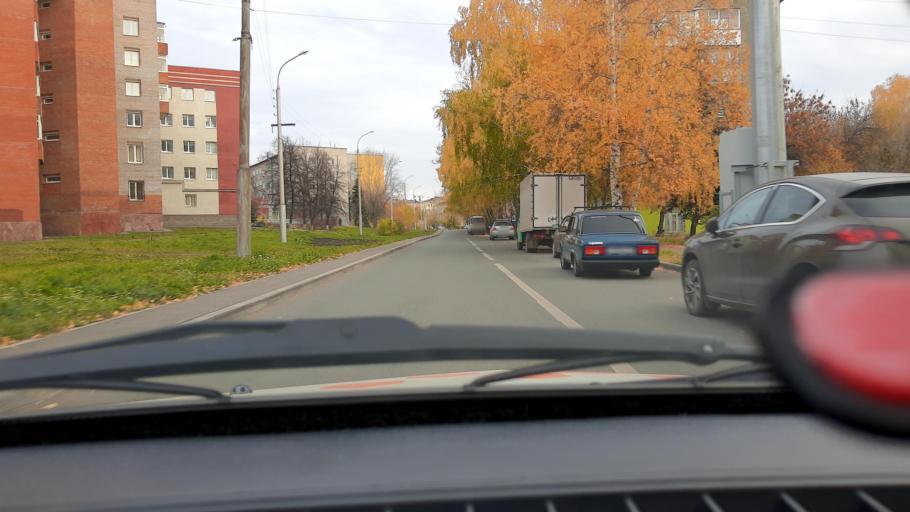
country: RU
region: Bashkortostan
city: Ufa
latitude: 54.8140
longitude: 56.0618
